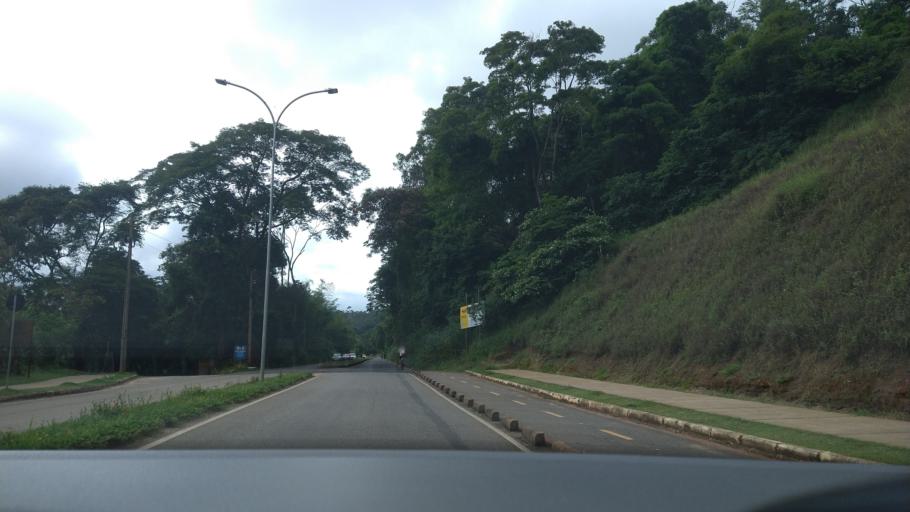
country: BR
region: Minas Gerais
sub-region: Vicosa
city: Vicosa
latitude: -20.7759
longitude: -42.8545
